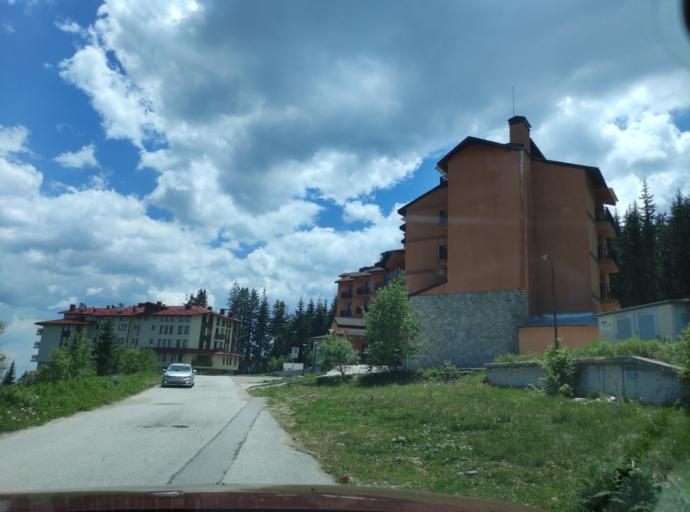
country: BG
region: Smolyan
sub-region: Obshtina Smolyan
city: Smolyan
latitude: 41.6363
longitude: 24.6983
